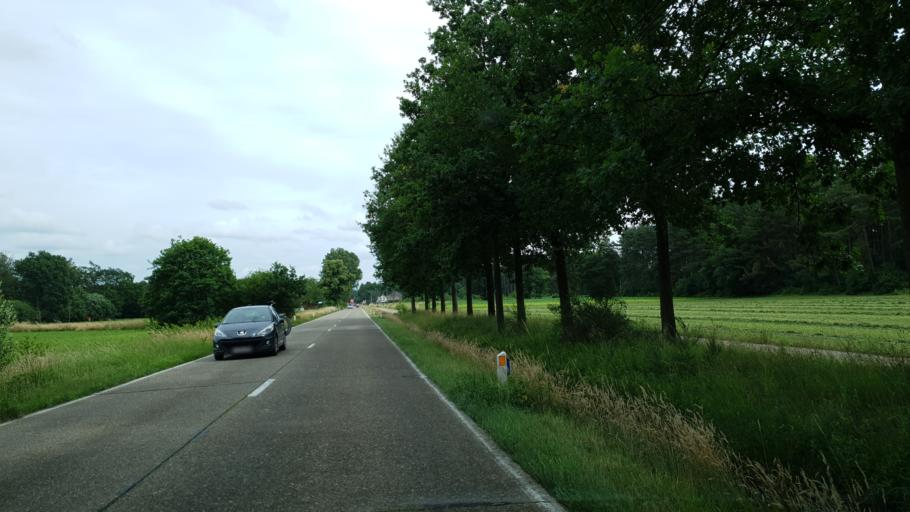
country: BE
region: Flanders
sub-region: Provincie Vlaams-Brabant
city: Scherpenheuvel-Zichem
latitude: 51.0463
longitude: 4.9526
